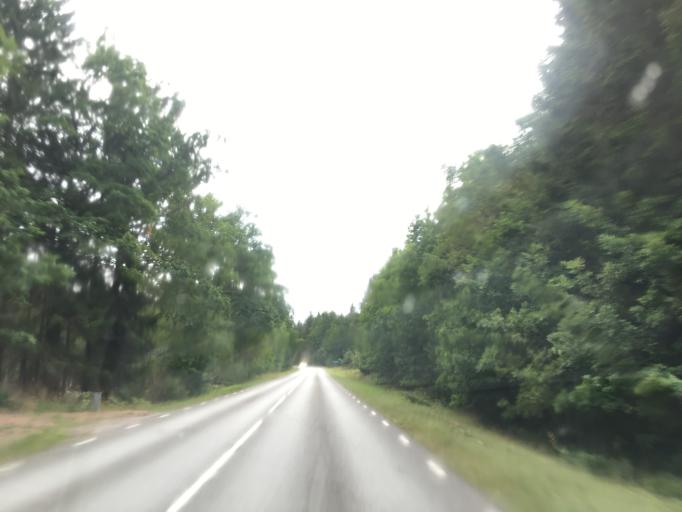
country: SE
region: Kalmar
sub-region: Nybro Kommun
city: Nybro
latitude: 56.8295
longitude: 15.9754
